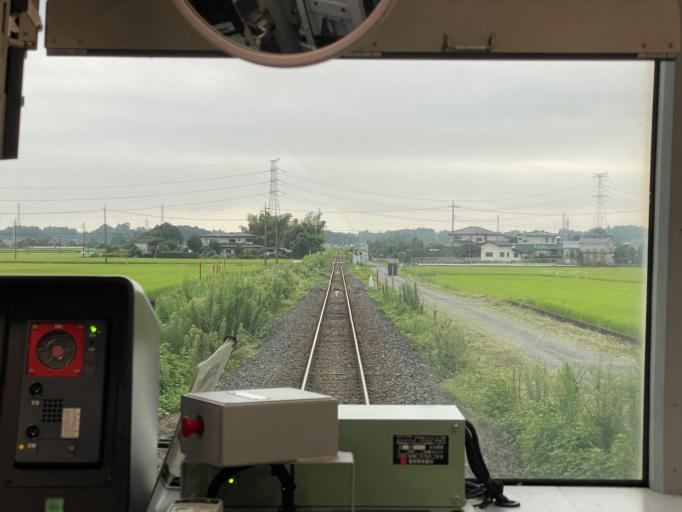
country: JP
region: Tochigi
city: Ujiie
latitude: 36.6491
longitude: 140.0066
